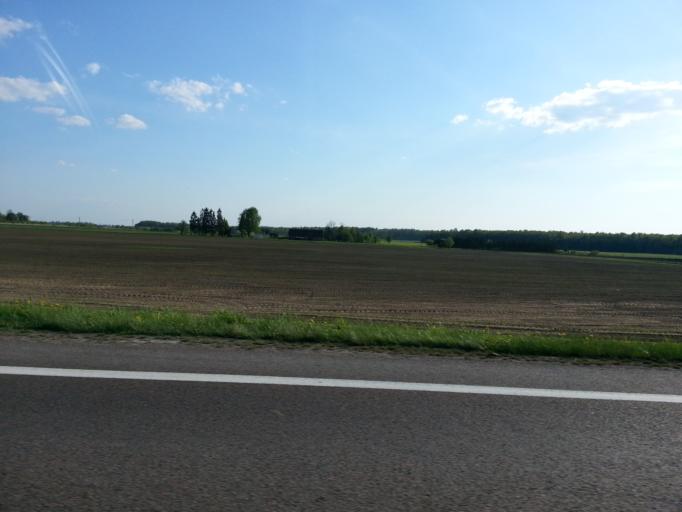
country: LT
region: Panevezys
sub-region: Panevezys City
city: Panevezys
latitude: 55.6674
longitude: 24.3549
